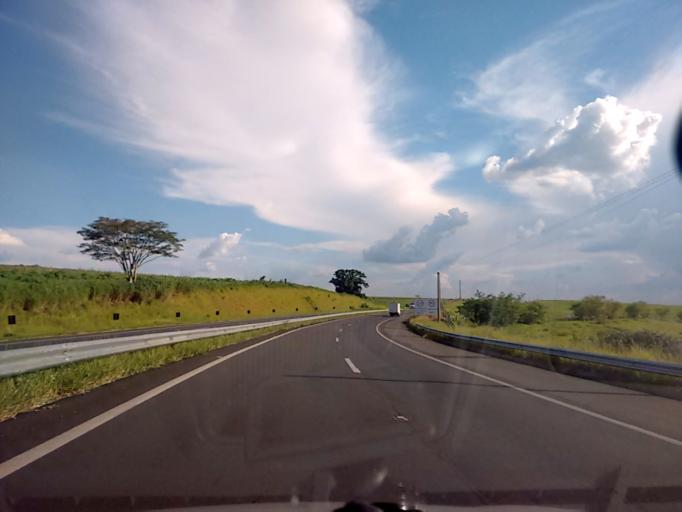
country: BR
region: Sao Paulo
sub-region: Duartina
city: Duartina
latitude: -22.2859
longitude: -49.4919
